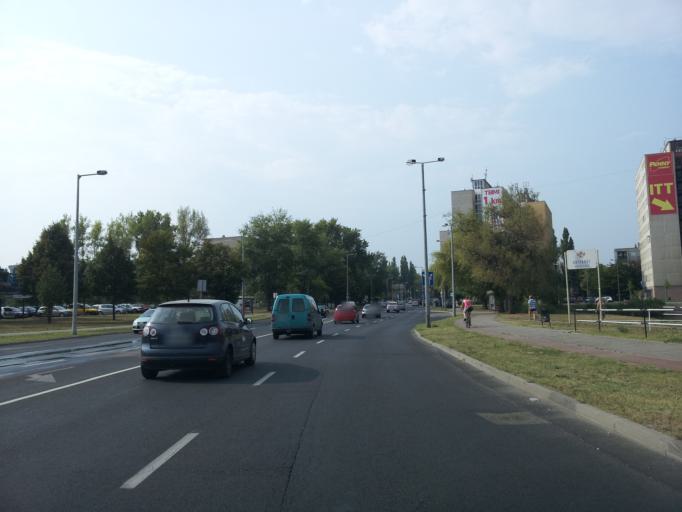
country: HU
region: Gyor-Moson-Sopron
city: Gyor
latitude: 47.6688
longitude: 17.6537
